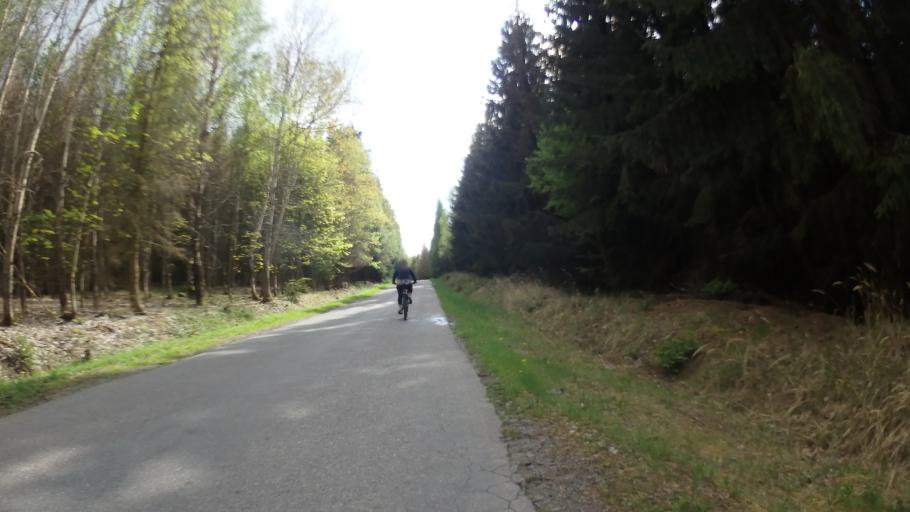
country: CZ
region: Vysocina
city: Merin
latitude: 49.3623
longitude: 15.8770
